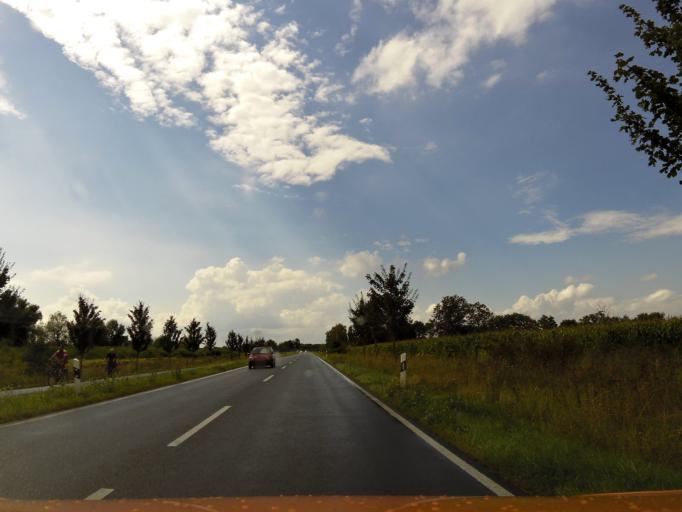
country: DE
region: Brandenburg
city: Ketzin
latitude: 52.4899
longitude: 12.8699
